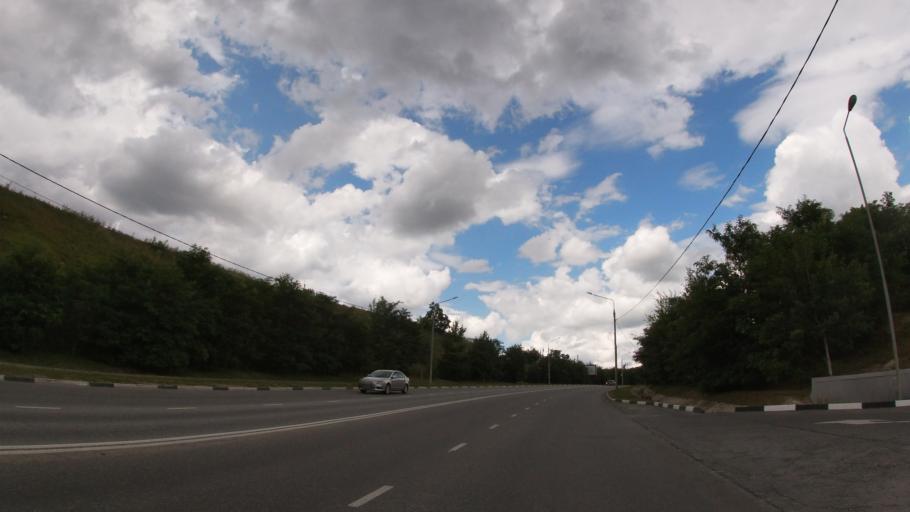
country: RU
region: Belgorod
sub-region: Belgorodskiy Rayon
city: Belgorod
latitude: 50.6103
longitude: 36.6128
